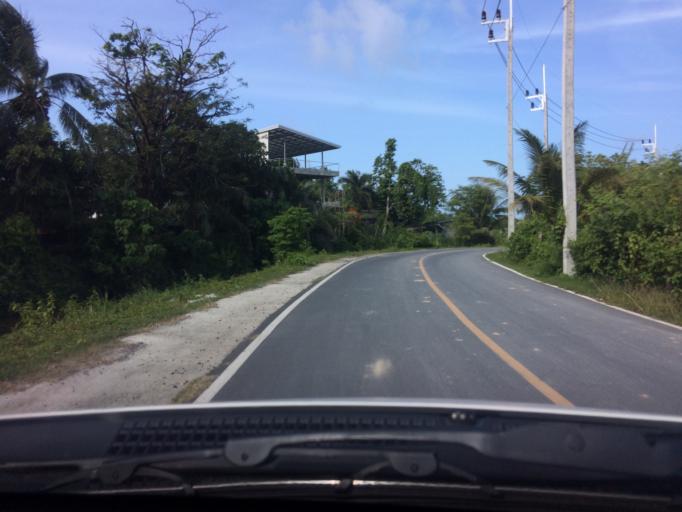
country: TH
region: Phuket
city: Thalang
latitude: 8.0441
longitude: 98.3287
